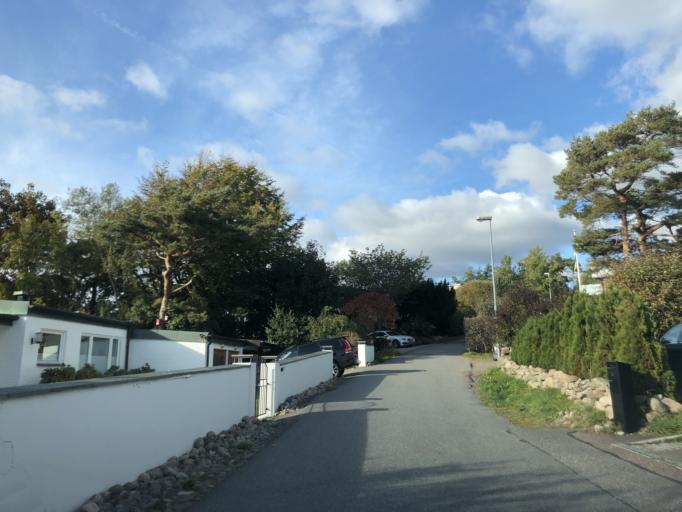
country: SE
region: Vaestra Goetaland
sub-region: Goteborg
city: Billdal
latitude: 57.6263
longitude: 11.9397
